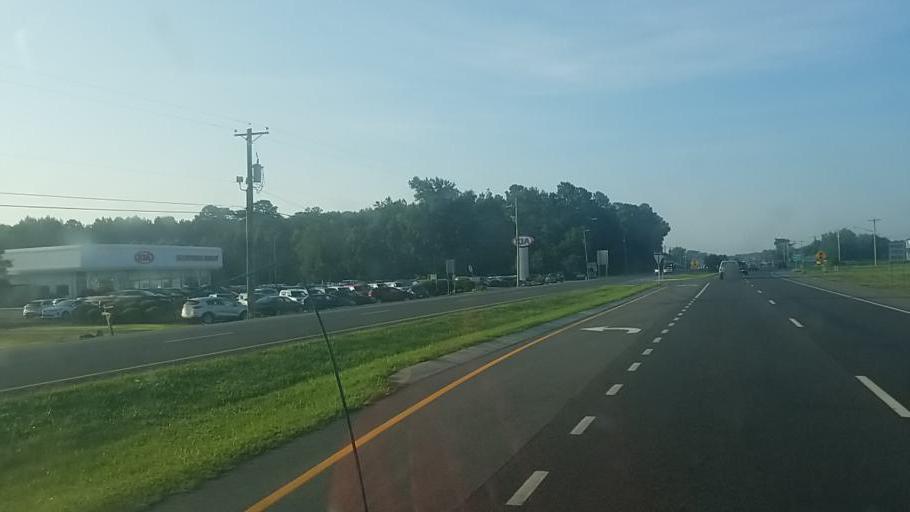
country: US
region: Delaware
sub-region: Sussex County
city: Selbyville
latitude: 38.4670
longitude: -75.2343
